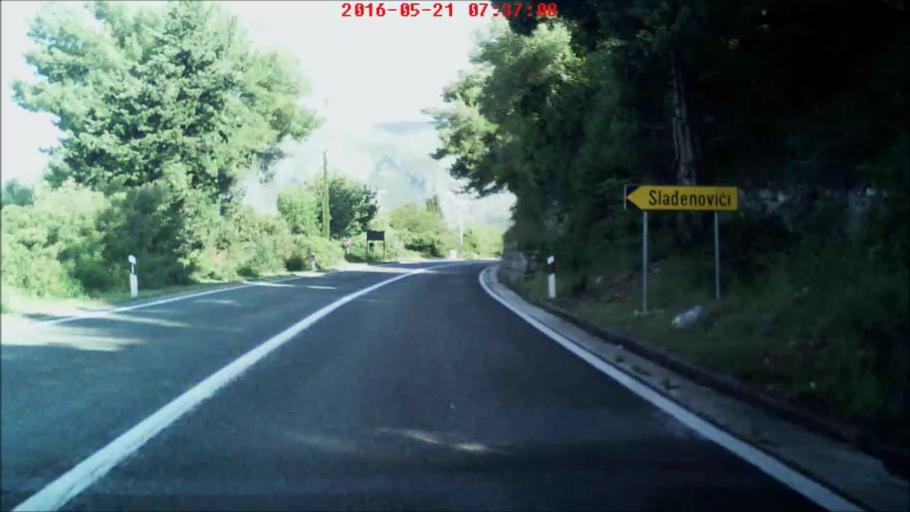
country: HR
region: Dubrovacko-Neretvanska
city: Podgora
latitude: 42.7872
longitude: 17.8564
